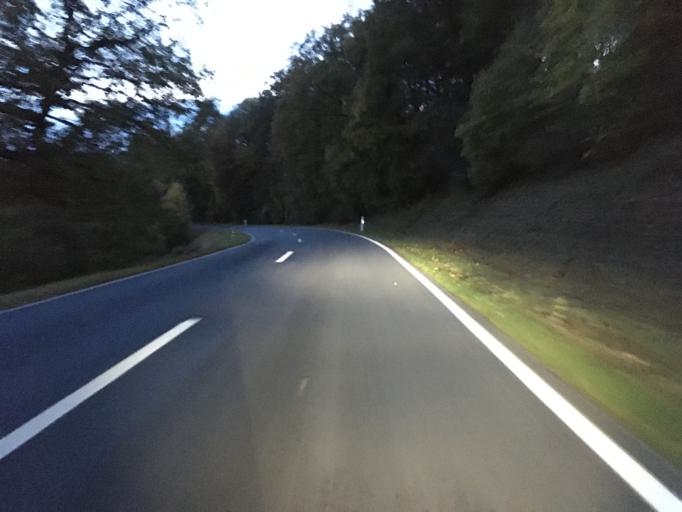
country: DE
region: Baden-Wuerttemberg
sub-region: Karlsruhe Region
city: Adelsheim
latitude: 49.3639
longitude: 9.4021
